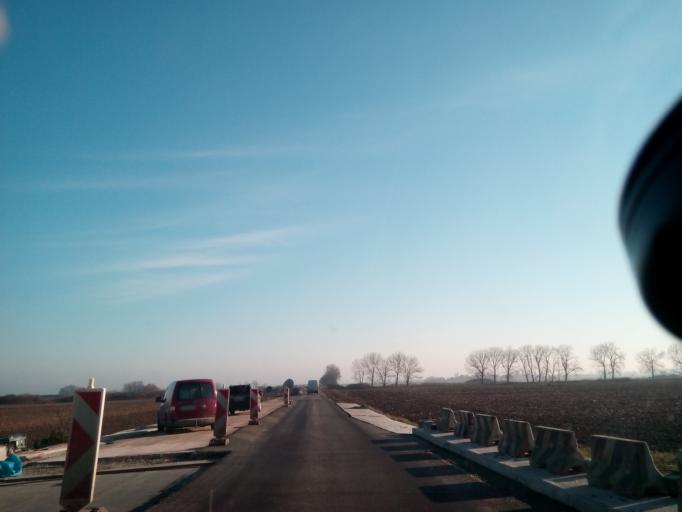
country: SK
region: Kosicky
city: Secovce
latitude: 48.6993
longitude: 21.7183
